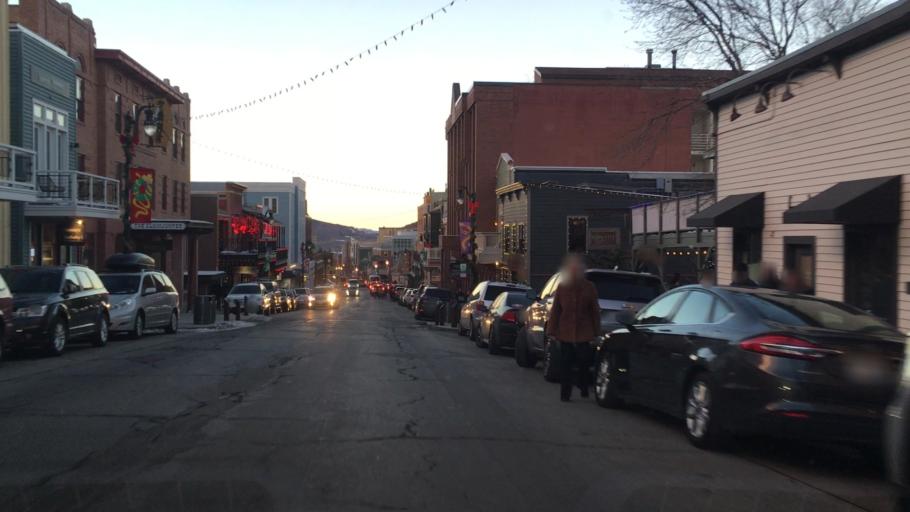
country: US
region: Utah
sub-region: Summit County
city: Park City
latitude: 40.6449
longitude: -111.4965
